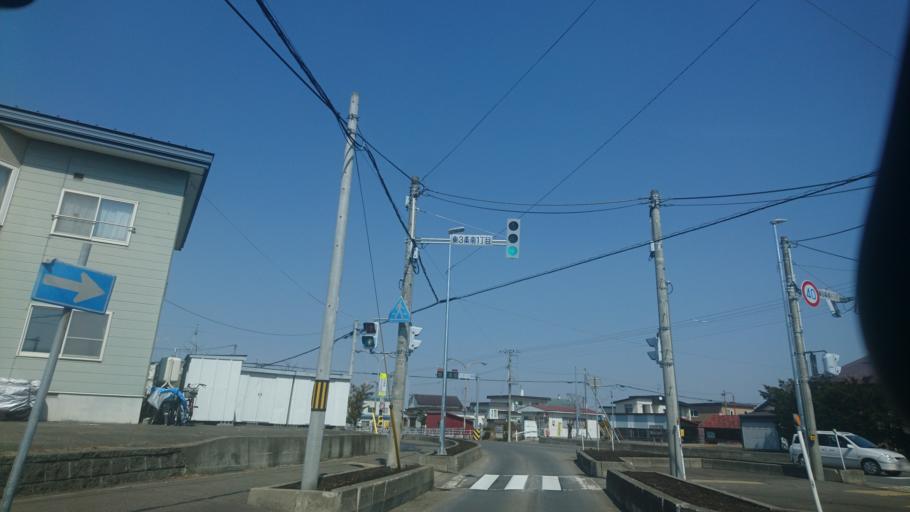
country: JP
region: Hokkaido
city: Obihiro
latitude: 42.9088
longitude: 143.0544
